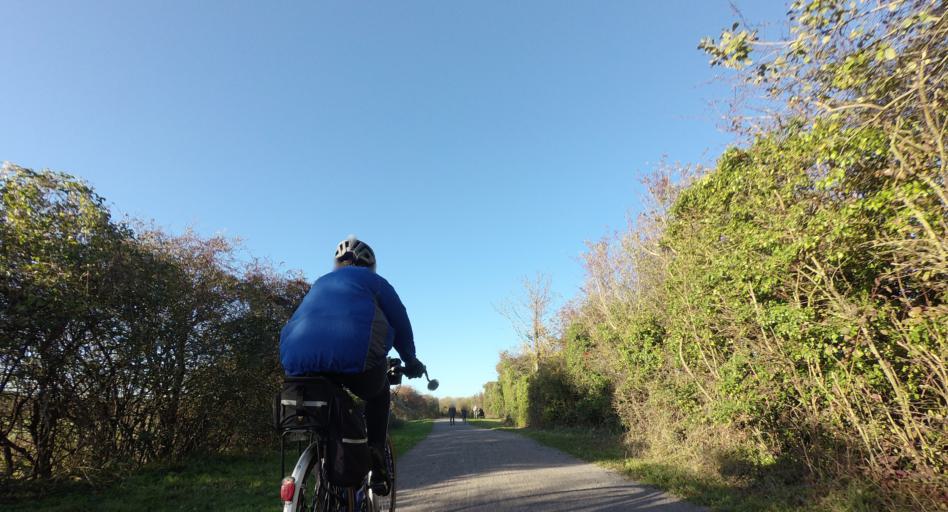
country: GB
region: England
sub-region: West Sussex
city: Shoreham-by-Sea
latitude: 50.8484
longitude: -0.2878
